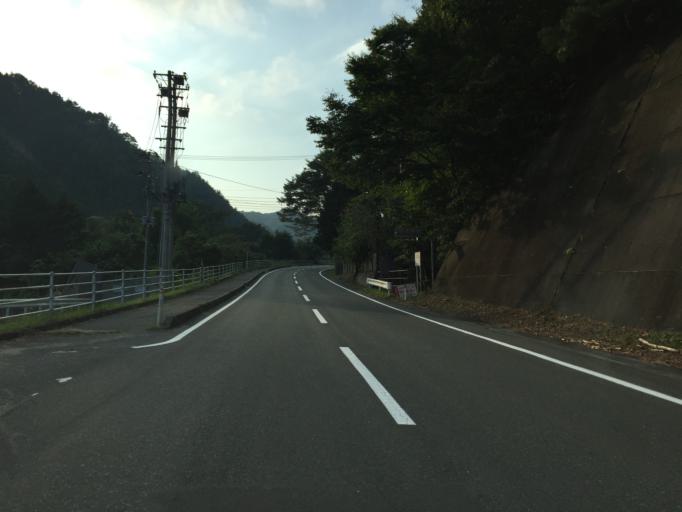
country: JP
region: Fukushima
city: Namie
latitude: 37.5401
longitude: 140.8651
